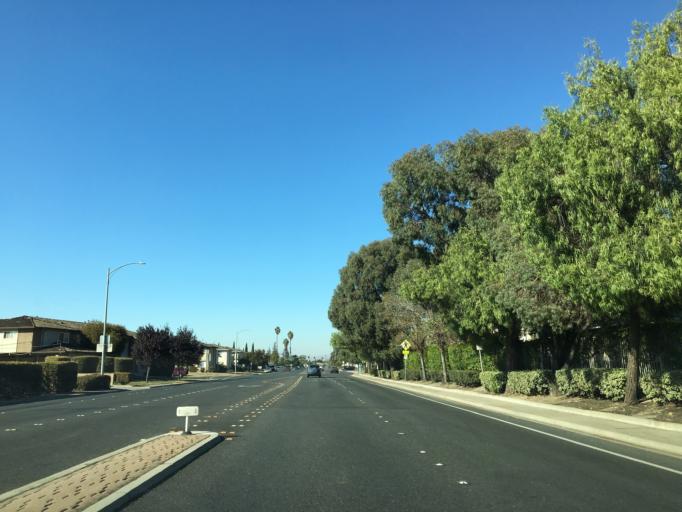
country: US
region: California
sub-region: Santa Clara County
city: Milpitas
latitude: 37.4335
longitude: -121.9097
